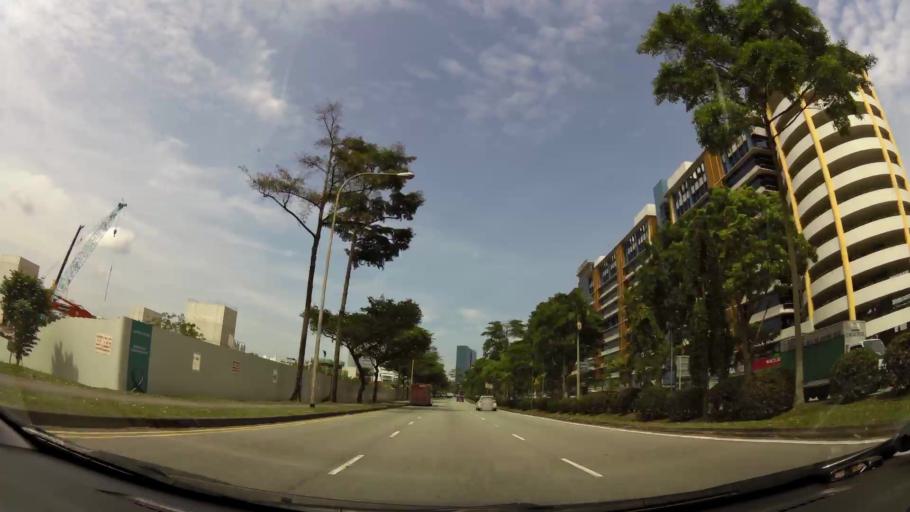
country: SG
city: Singapore
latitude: 1.3266
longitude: 103.7546
